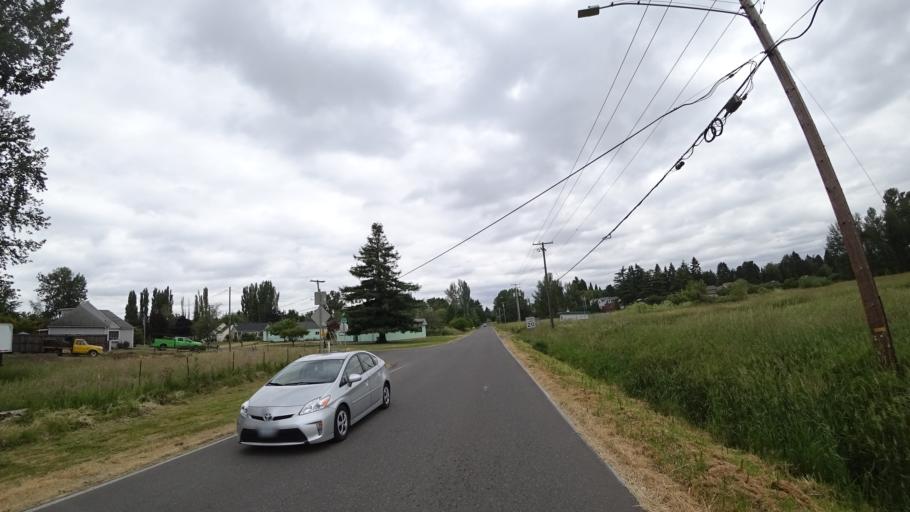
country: US
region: Washington
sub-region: Clark County
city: Vancouver
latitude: 45.5922
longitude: -122.6519
